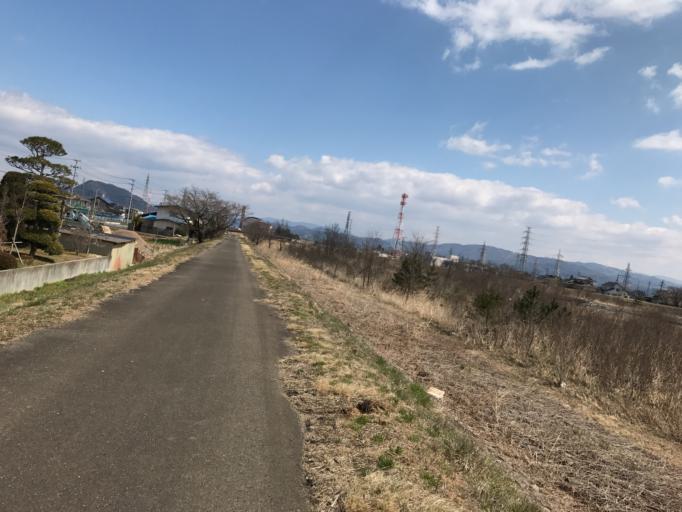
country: JP
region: Fukushima
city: Fukushima-shi
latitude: 37.7496
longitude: 140.4126
